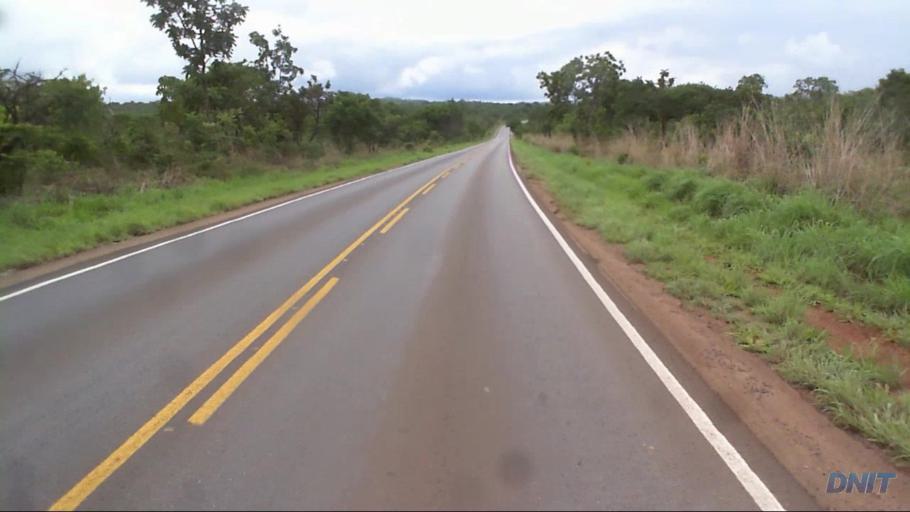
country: BR
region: Goias
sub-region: Padre Bernardo
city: Padre Bernardo
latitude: -15.3940
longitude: -48.2017
